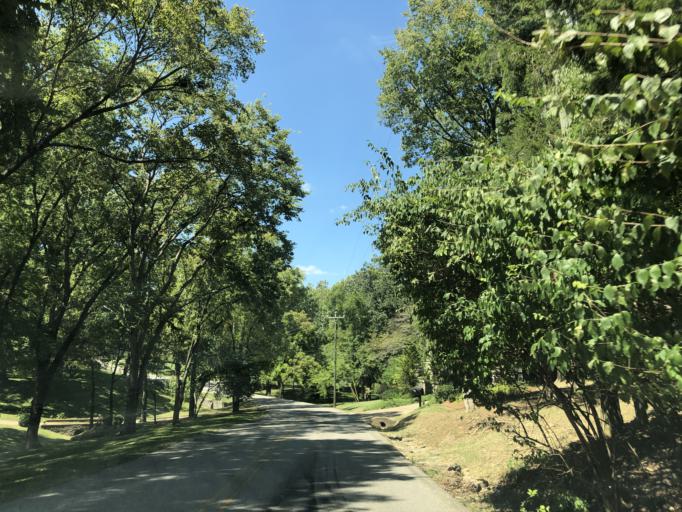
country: US
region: Tennessee
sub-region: Davidson County
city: Oak Hill
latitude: 36.0766
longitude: -86.7909
